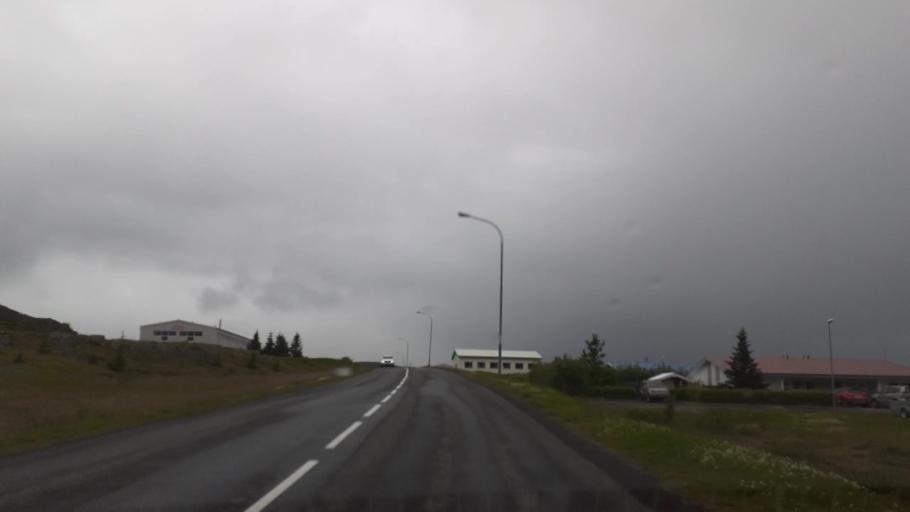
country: IS
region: East
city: Egilsstadir
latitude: 65.7527
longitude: -14.8356
